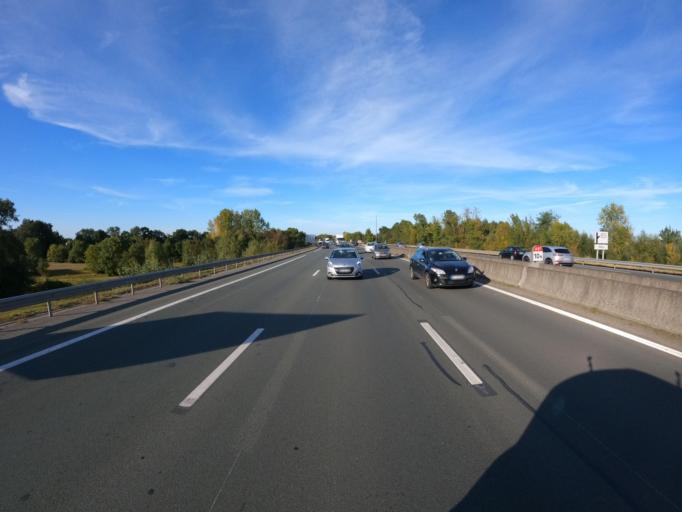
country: FR
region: Pays de la Loire
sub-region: Departement de Maine-et-Loire
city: Les Ponts-de-Ce
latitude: 47.4219
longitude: -0.5043
